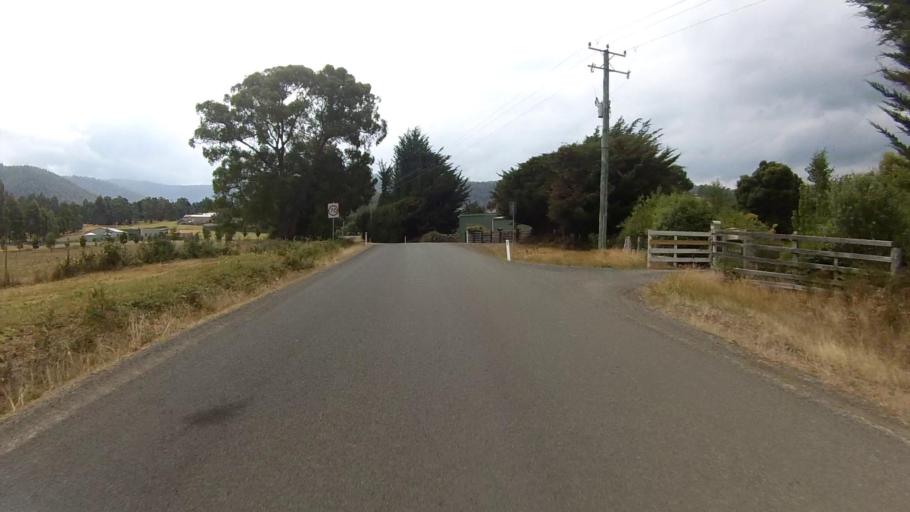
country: AU
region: Tasmania
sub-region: Huon Valley
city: Huonville
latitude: -42.9839
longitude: 147.0573
